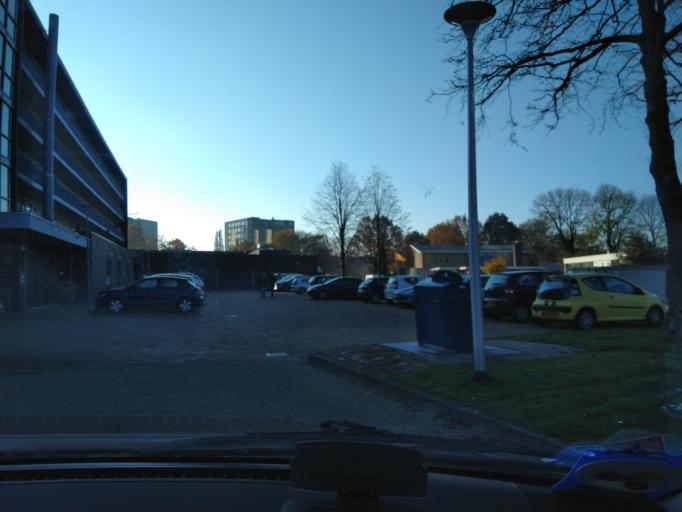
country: NL
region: Drenthe
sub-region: Gemeente Assen
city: Assen
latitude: 53.0014
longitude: 6.5482
